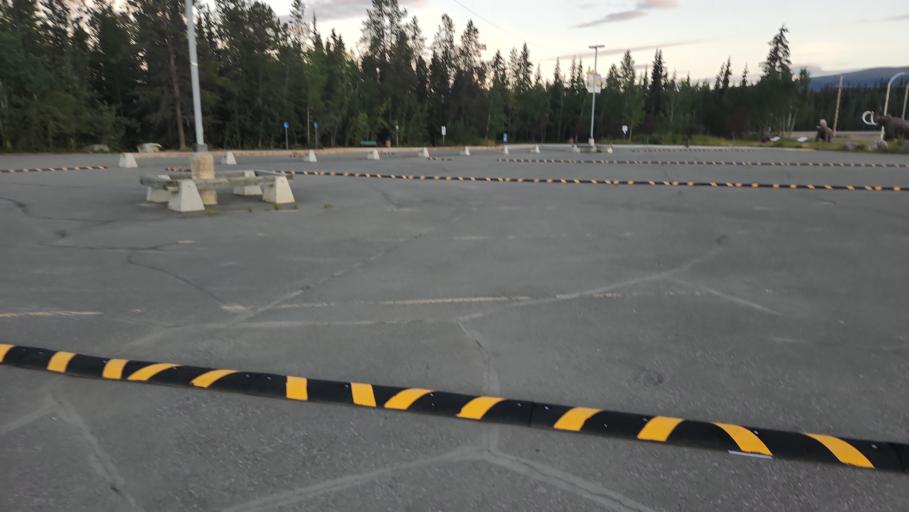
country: CA
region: Yukon
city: Whitehorse
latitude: 60.7106
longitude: -135.0799
